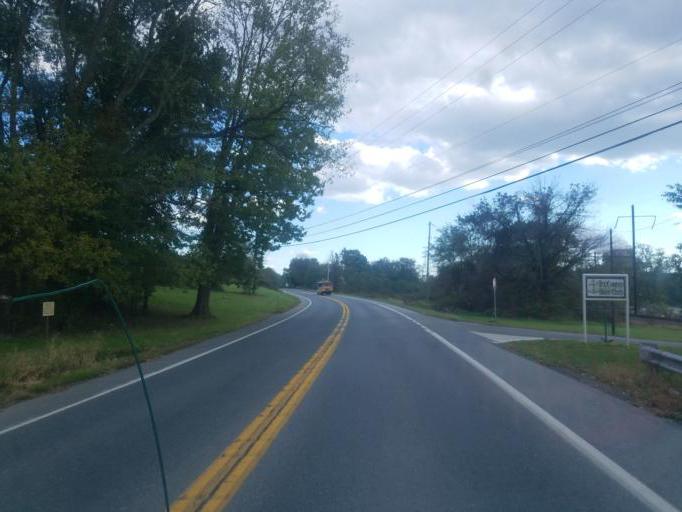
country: US
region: Pennsylvania
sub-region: Dauphin County
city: Middletown
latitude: 40.1703
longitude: -76.7229
